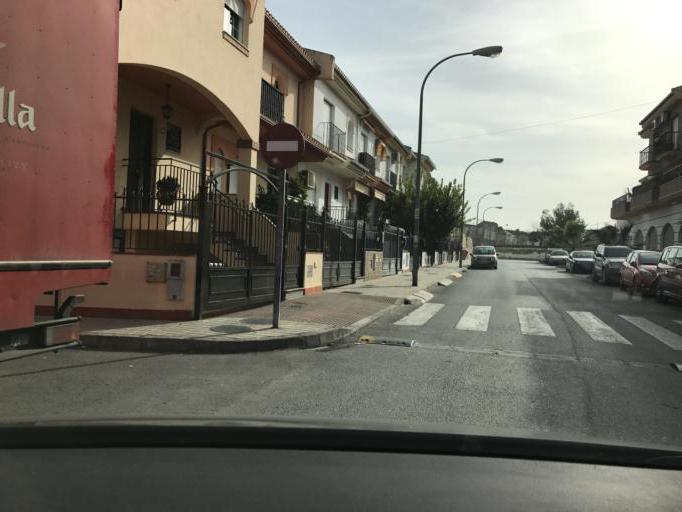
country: ES
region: Andalusia
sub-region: Provincia de Granada
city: Atarfe
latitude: 37.1904
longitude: -3.7142
